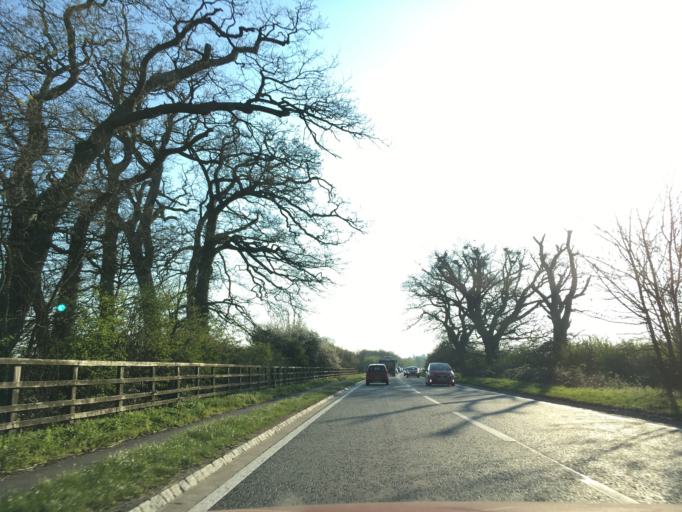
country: GB
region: England
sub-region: Oxfordshire
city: North Leigh
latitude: 51.7903
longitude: -1.4288
